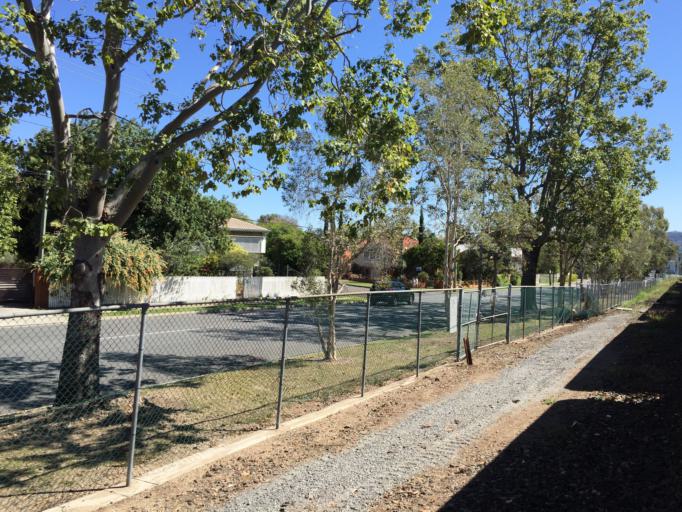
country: AU
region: Queensland
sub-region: Brisbane
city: Rocklea
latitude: -27.5258
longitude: 152.9783
